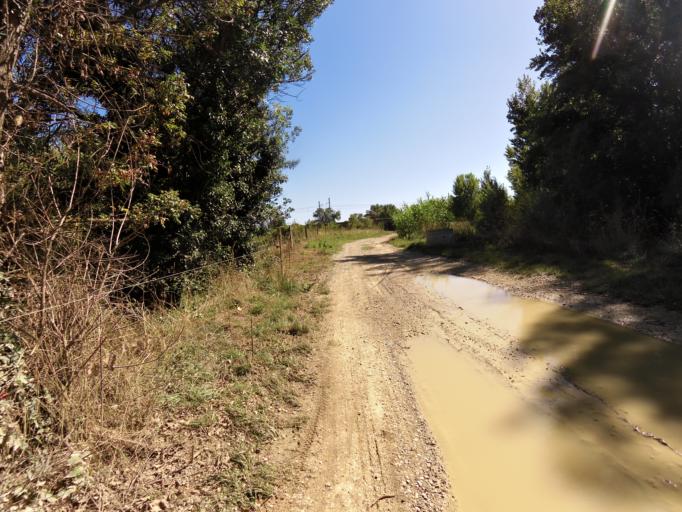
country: FR
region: Languedoc-Roussillon
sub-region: Departement du Gard
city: Vergeze
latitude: 43.7388
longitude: 4.2140
